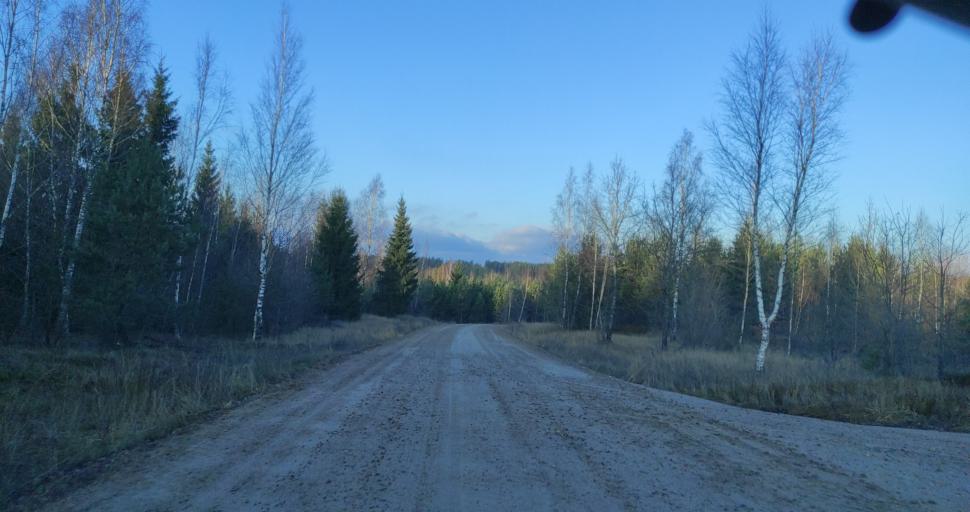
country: LV
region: Kuldigas Rajons
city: Kuldiga
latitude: 57.0575
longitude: 21.8658
